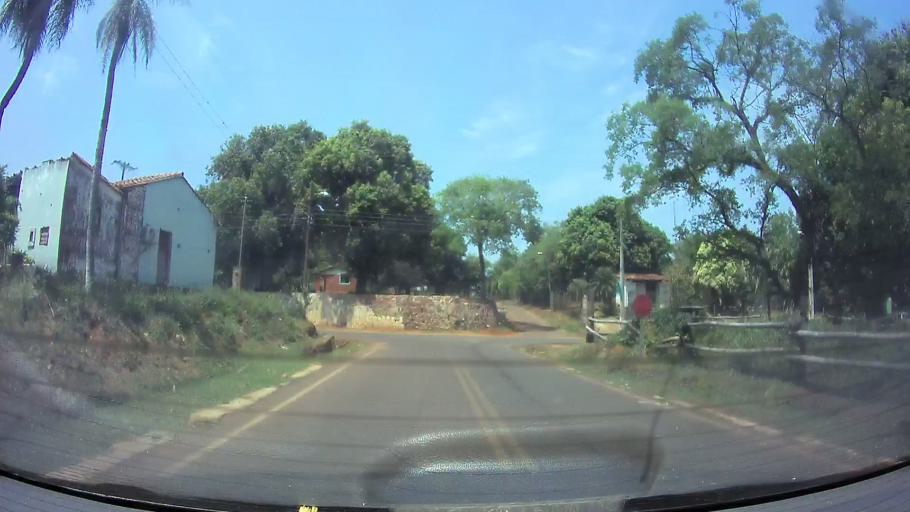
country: PY
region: Central
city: Ita
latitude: -25.4405
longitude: -57.4012
